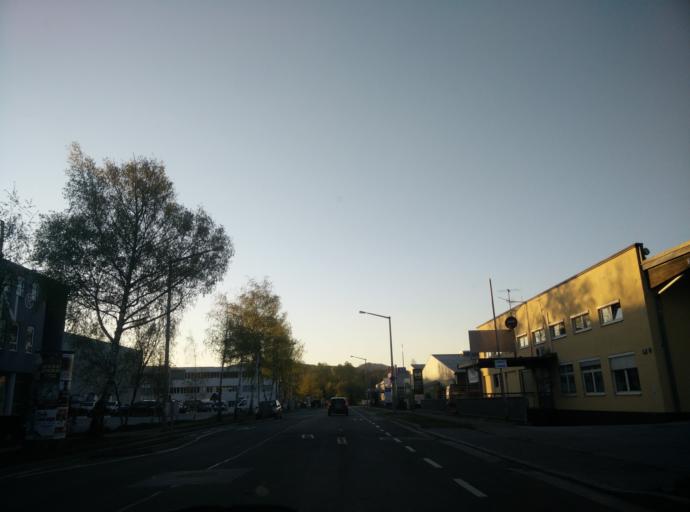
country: AT
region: Salzburg
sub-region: Salzburg Stadt
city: Salzburg
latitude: 47.8230
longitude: 13.0652
